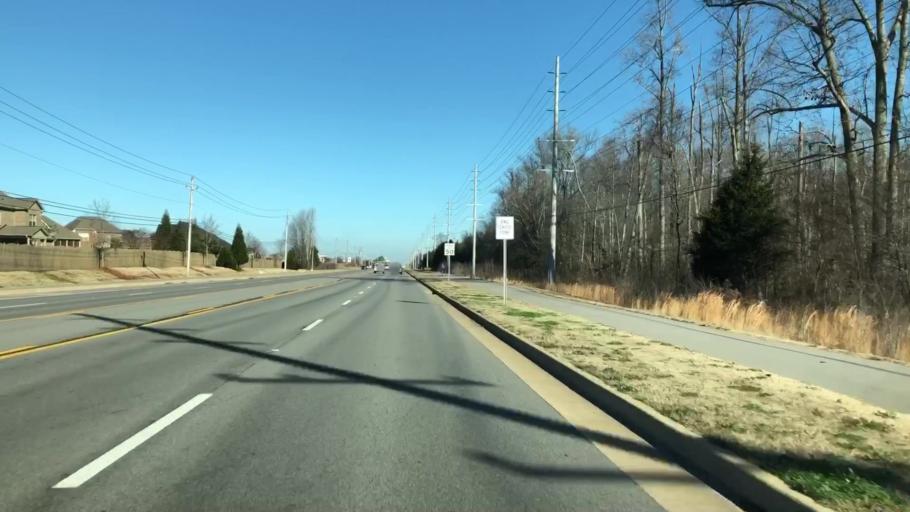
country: US
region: Alabama
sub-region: Madison County
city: Madison
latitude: 34.7233
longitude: -86.7864
